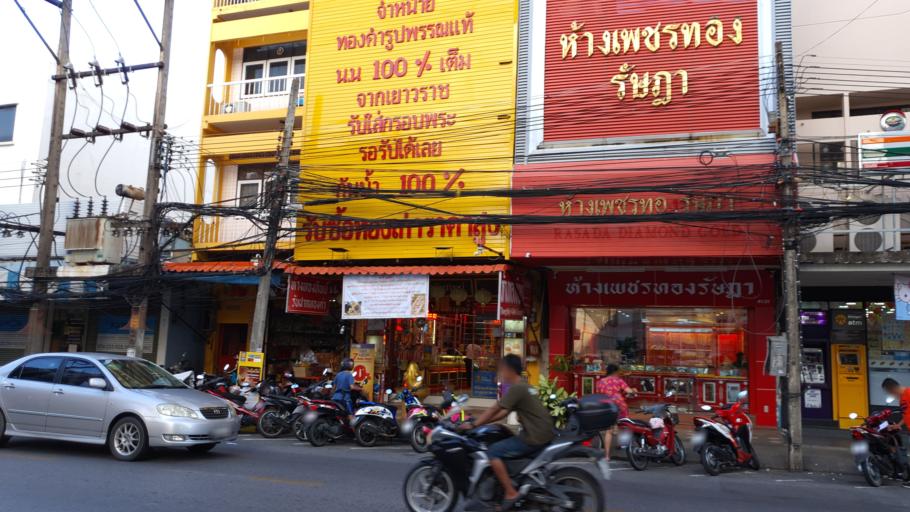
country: TH
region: Phuket
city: Ban Talat Nua
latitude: 7.8823
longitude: 98.3925
